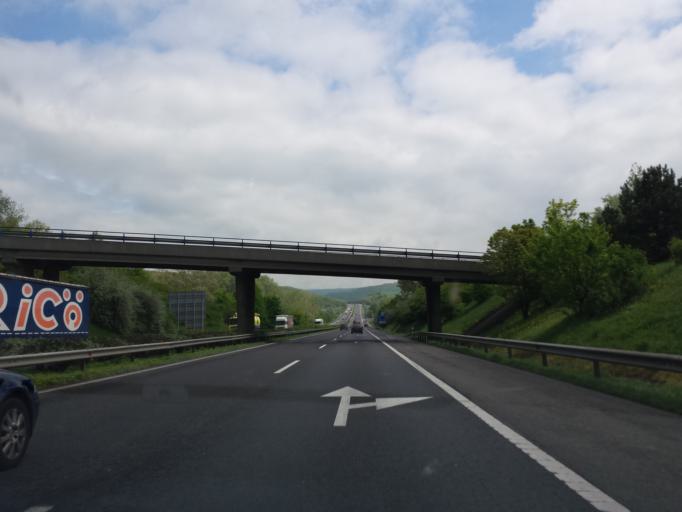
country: HU
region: Komarom-Esztergom
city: Tatabanya
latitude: 47.5767
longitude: 18.4256
